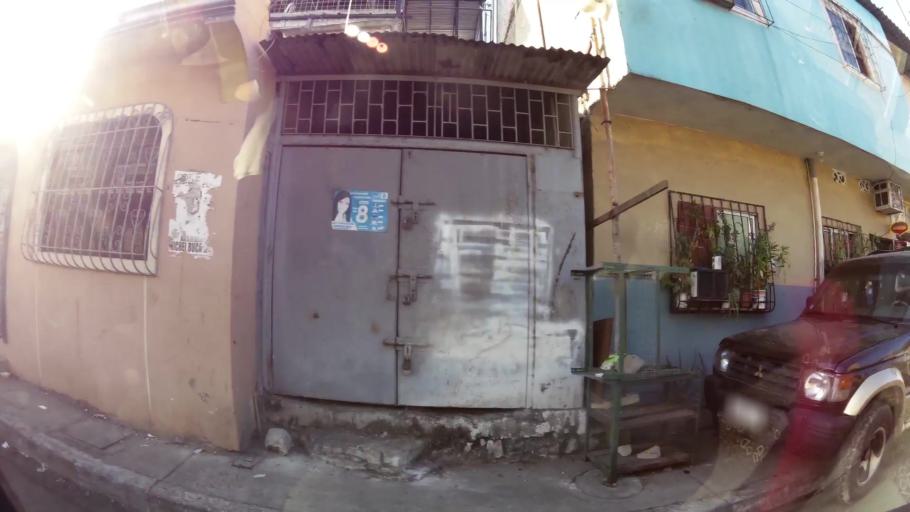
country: EC
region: Guayas
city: Guayaquil
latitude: -2.2247
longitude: -79.9090
